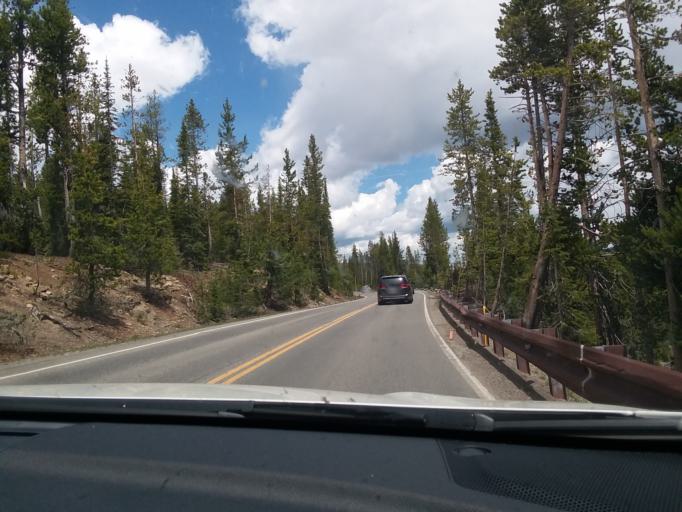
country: US
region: Montana
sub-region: Gallatin County
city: West Yellowstone
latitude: 44.2062
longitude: -110.6610
